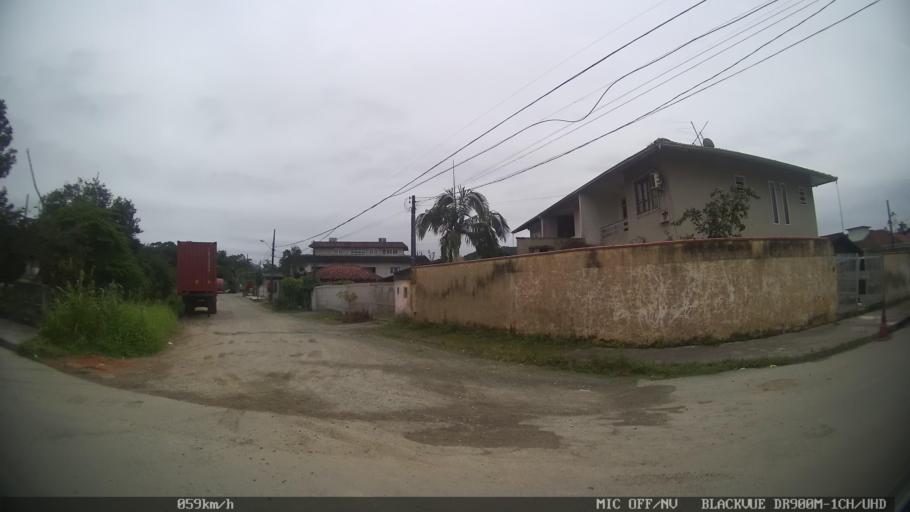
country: BR
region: Santa Catarina
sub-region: Joinville
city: Joinville
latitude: -26.2663
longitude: -48.8872
